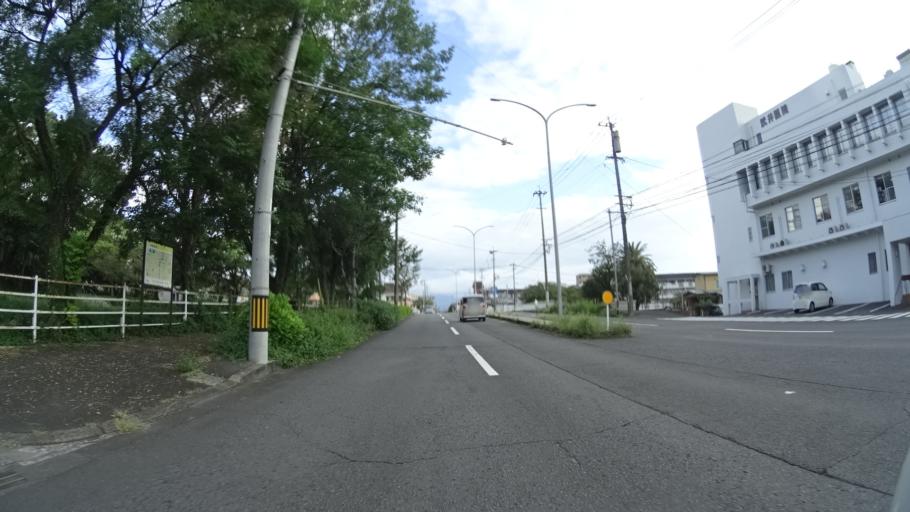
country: JP
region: Oita
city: Beppu
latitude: 33.2876
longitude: 131.4963
